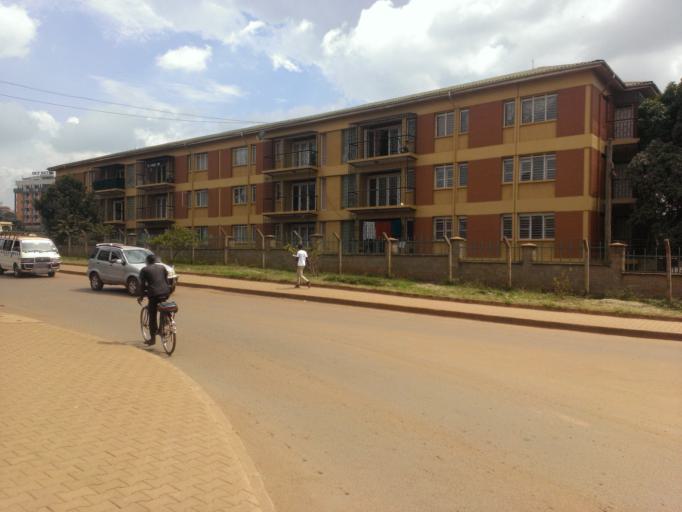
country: UG
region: Central Region
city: Kampala Central Division
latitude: 0.3191
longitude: 32.5689
